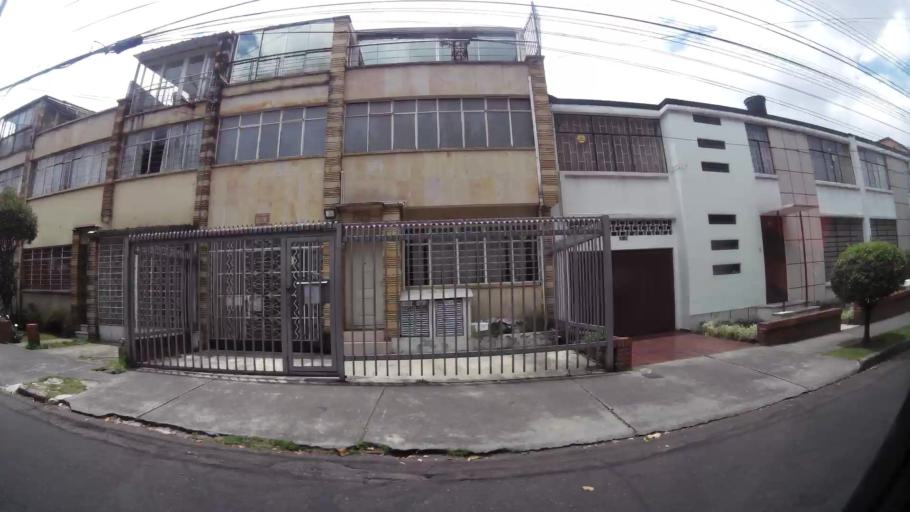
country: CO
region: Bogota D.C.
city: Bogota
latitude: 4.6282
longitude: -74.0769
